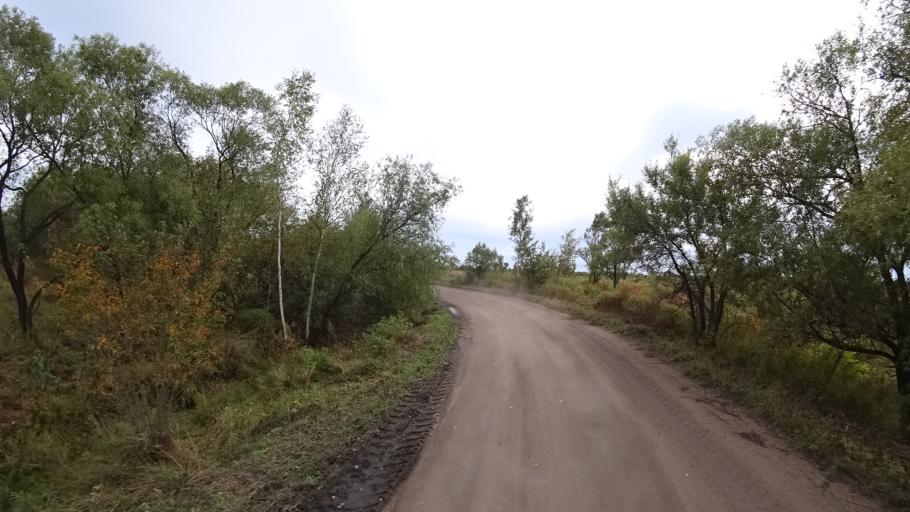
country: RU
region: Amur
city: Arkhara
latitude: 49.3474
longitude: 130.0976
